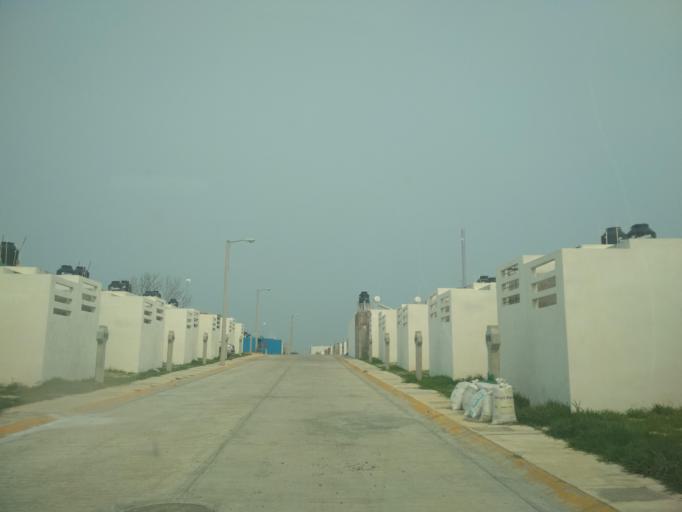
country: MX
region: Veracruz
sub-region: Veracruz
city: Las Amapolas
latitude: 19.1394
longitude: -96.2251
